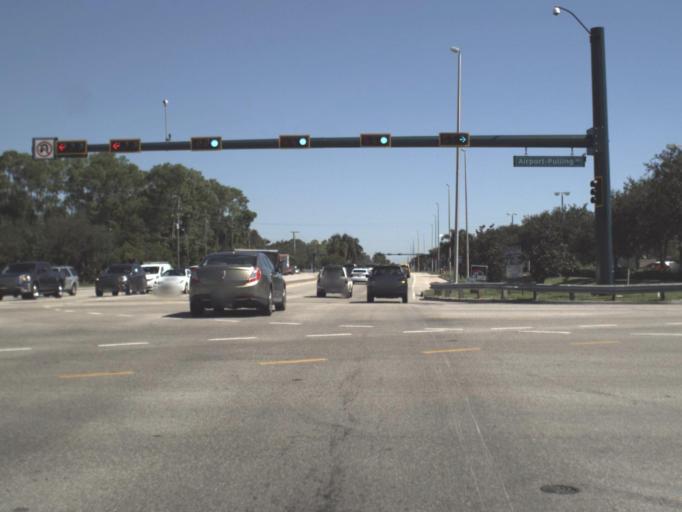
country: US
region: Florida
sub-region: Collier County
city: Pine Ridge
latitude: 26.2116
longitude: -81.7686
